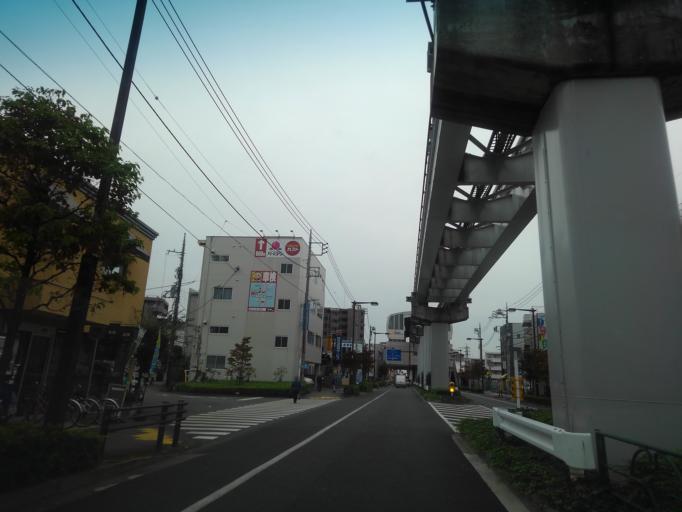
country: JP
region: Tokyo
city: Higashimurayama-shi
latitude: 35.7407
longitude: 139.4164
